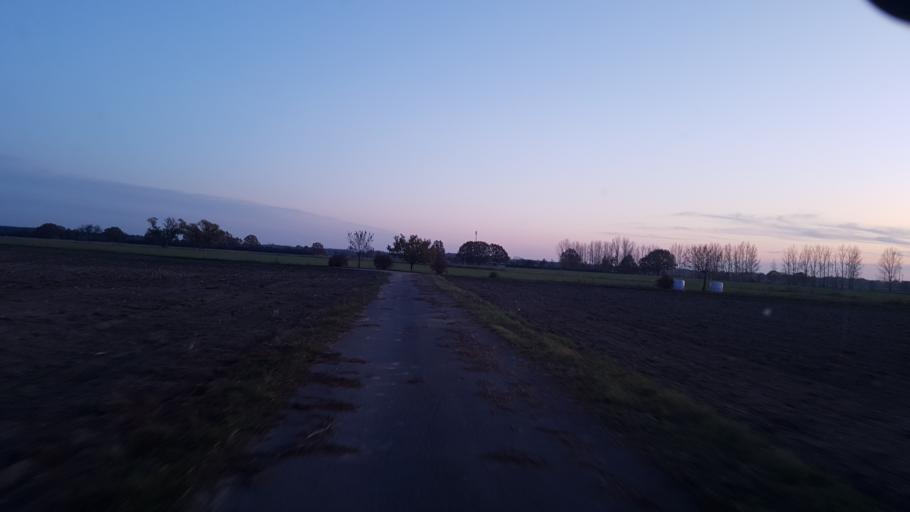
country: DE
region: Brandenburg
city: Schilda
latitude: 51.6226
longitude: 13.3314
